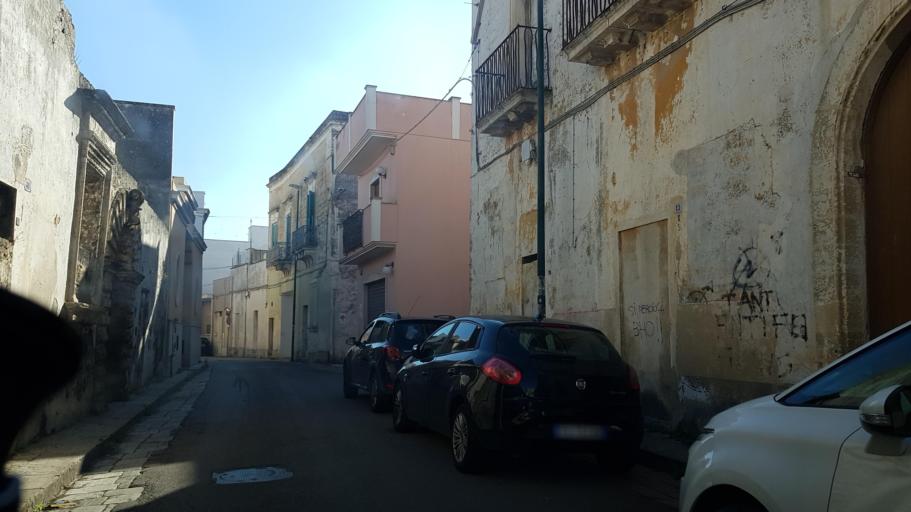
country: IT
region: Apulia
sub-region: Provincia di Lecce
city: Novoli
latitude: 40.3755
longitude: 18.0502
